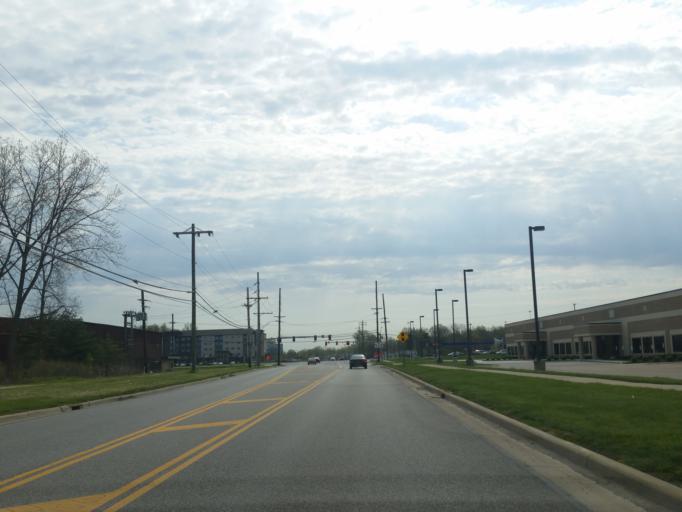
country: US
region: Ohio
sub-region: Lorain County
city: Avon Center
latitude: 41.4674
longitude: -81.9915
